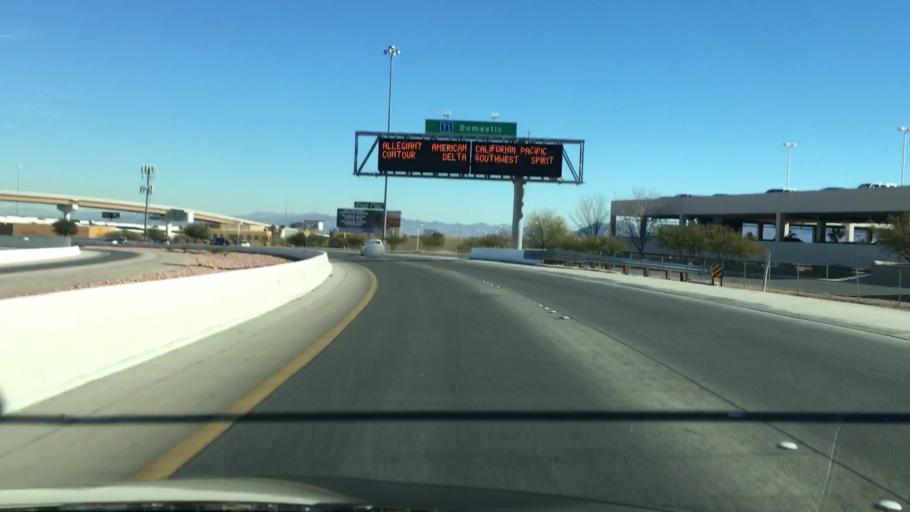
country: US
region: Nevada
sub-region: Clark County
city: Paradise
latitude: 36.0611
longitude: -115.1534
